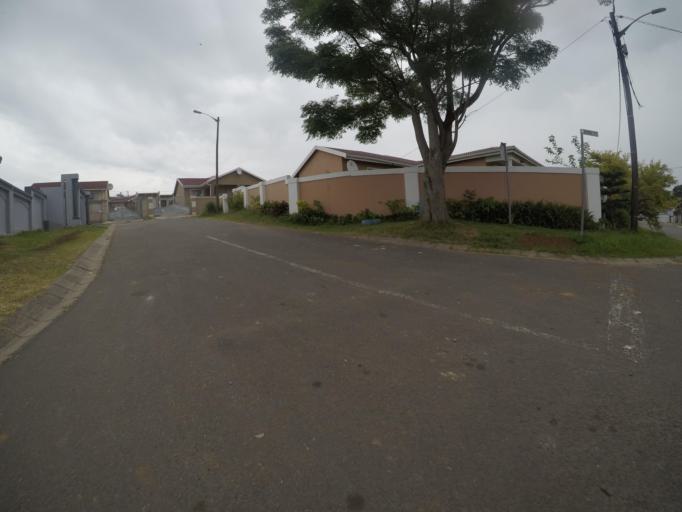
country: ZA
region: Eastern Cape
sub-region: Buffalo City Metropolitan Municipality
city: East London
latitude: -32.9934
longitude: 27.8462
